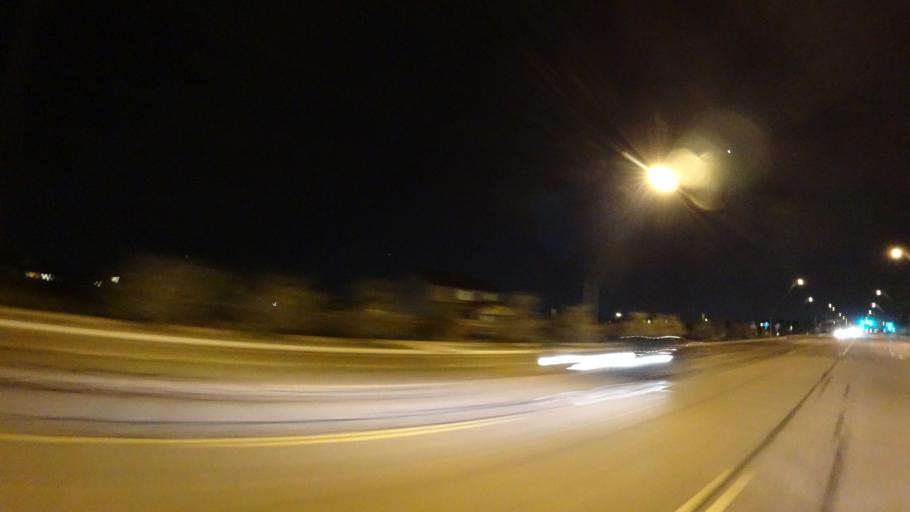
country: US
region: Arizona
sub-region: Pinal County
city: Apache Junction
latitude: 33.4224
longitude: -111.6603
